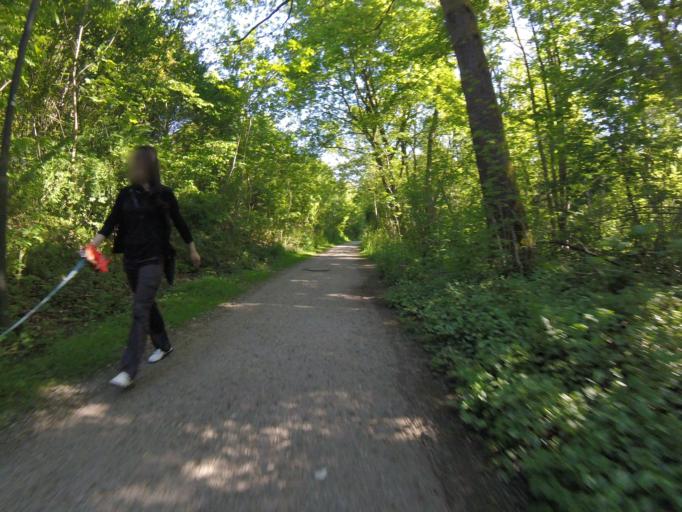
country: DE
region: Bavaria
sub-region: Upper Bavaria
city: Neubiberg
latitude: 48.0743
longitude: 11.6575
